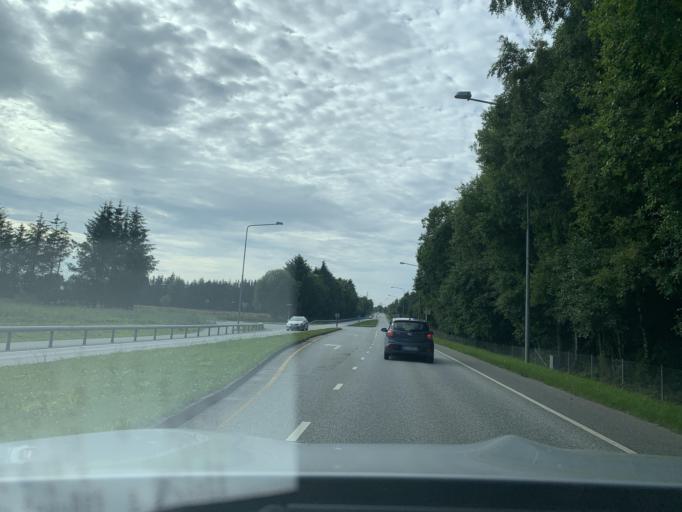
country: NO
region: Rogaland
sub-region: Stavanger
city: Stavanger
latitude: 58.9167
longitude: 5.7191
